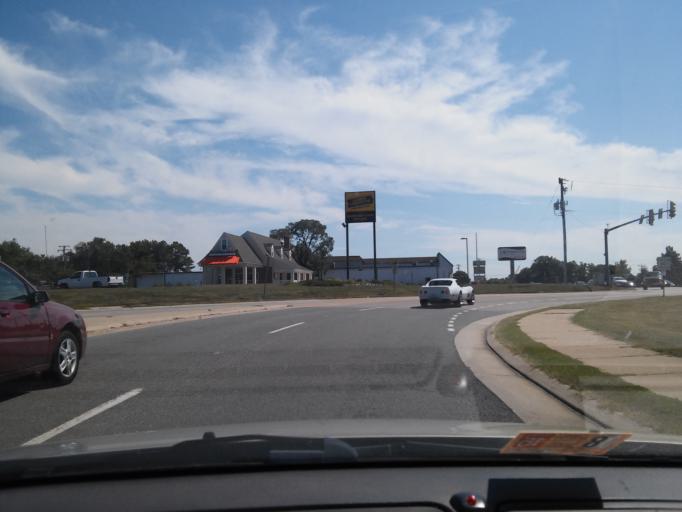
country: US
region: Virginia
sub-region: Chesterfield County
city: Bon Air
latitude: 37.5065
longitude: -77.5799
